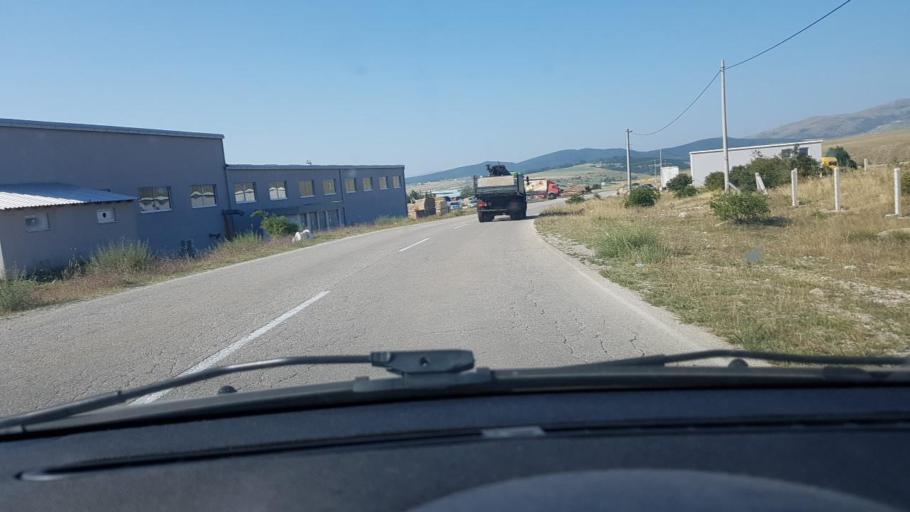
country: BA
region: Federation of Bosnia and Herzegovina
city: Tomislavgrad
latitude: 43.7711
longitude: 17.2363
